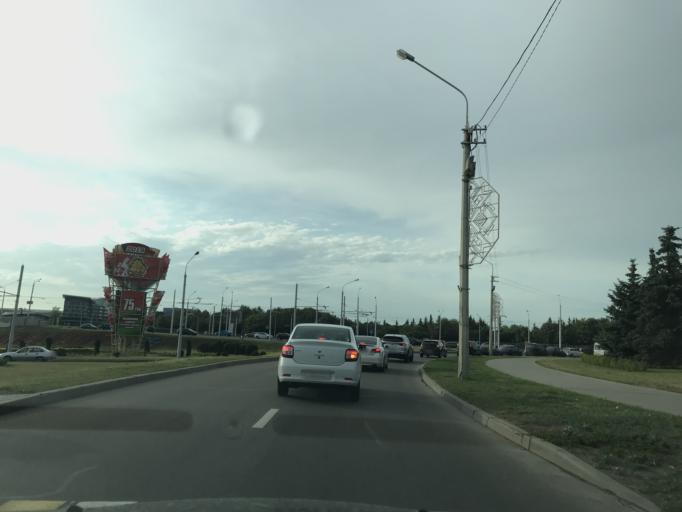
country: BY
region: Minsk
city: Minsk
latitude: 53.9281
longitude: 27.5172
